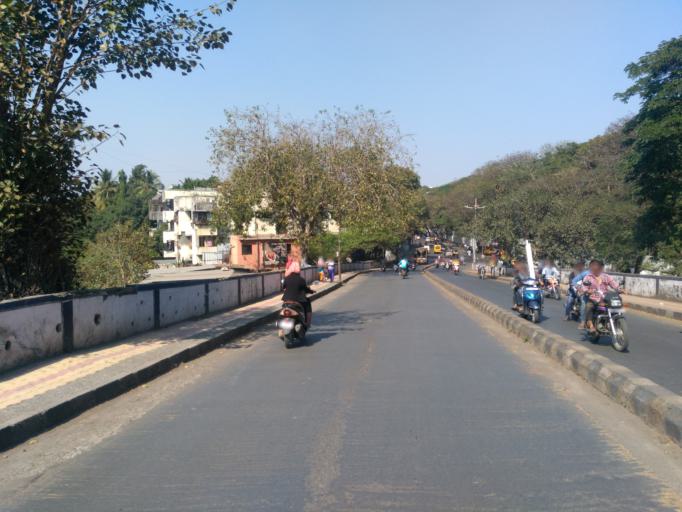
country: IN
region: Maharashtra
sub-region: Pune Division
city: Pune
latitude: 18.5004
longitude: 73.8507
